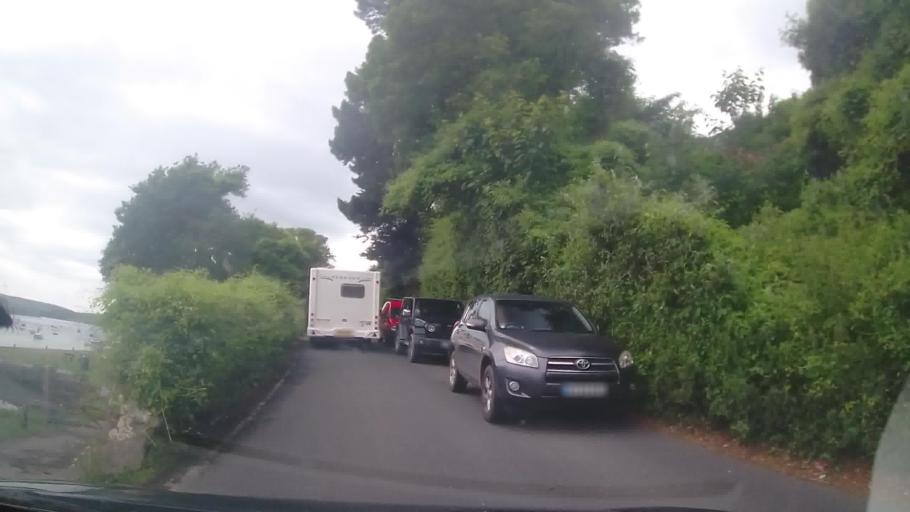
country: GB
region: England
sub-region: Devon
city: Kingsbridge
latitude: 50.2752
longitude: -3.7632
